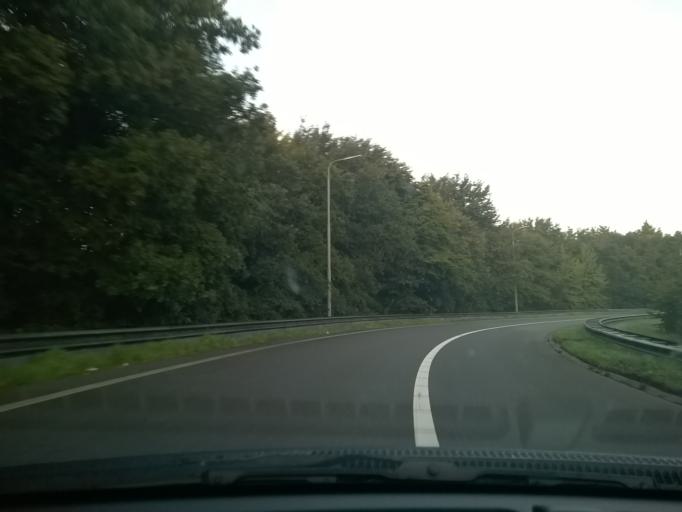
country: NL
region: North Holland
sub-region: Gemeente Laren
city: Laren
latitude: 52.2298
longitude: 5.2383
